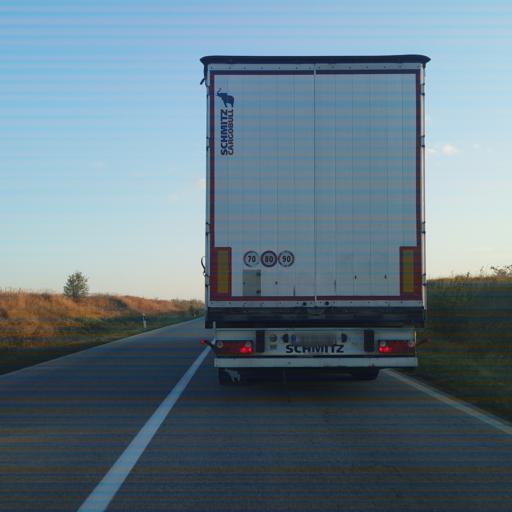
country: RS
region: Central Serbia
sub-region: Zajecarski Okrug
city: Zajecar
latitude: 44.0631
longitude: 22.3339
